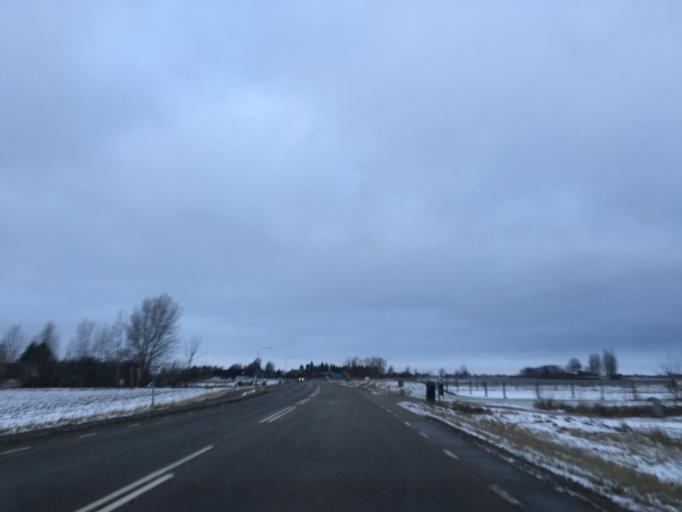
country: SE
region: Skane
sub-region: Vellinge Kommun
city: Hollviken
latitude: 55.4333
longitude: 12.9842
